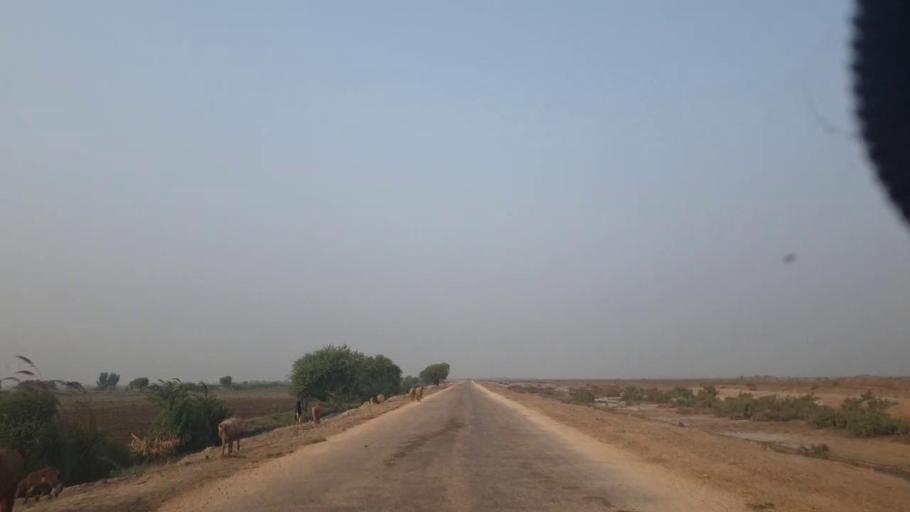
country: PK
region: Sindh
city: Bulri
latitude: 24.8450
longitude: 68.4042
